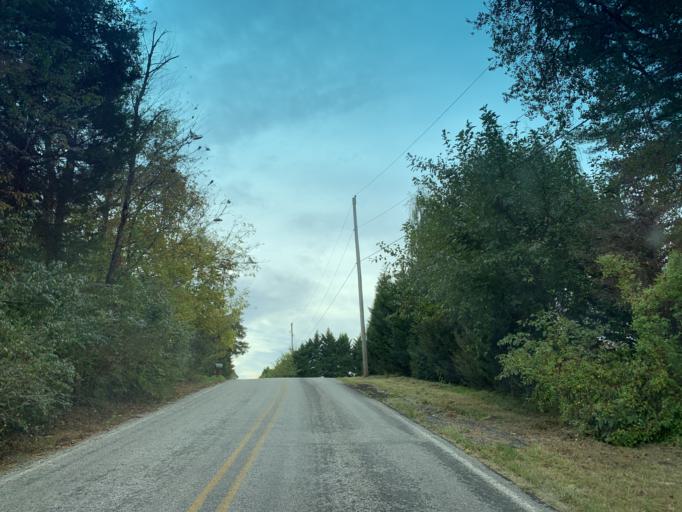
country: US
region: Pennsylvania
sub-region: York County
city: Stewartstown
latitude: 39.8103
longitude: -76.4881
